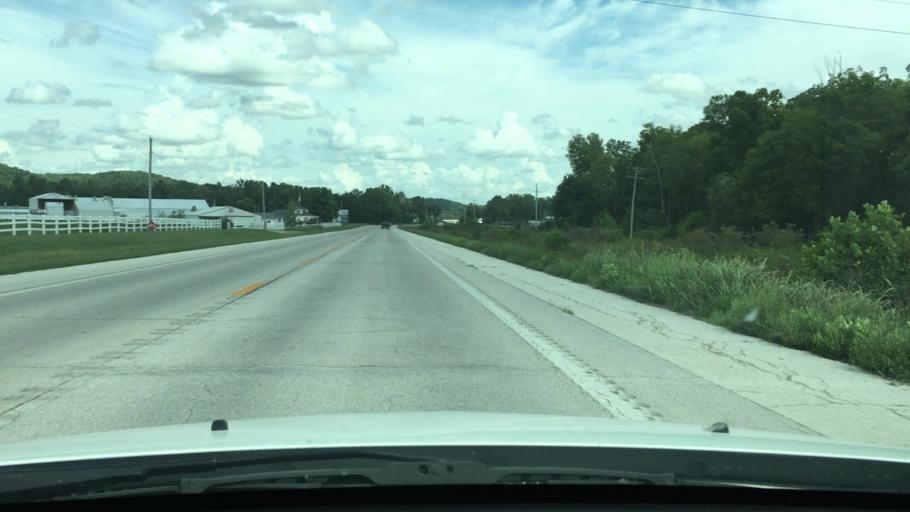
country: US
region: Missouri
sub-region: Pike County
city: Louisiana
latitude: 39.4065
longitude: -91.1055
